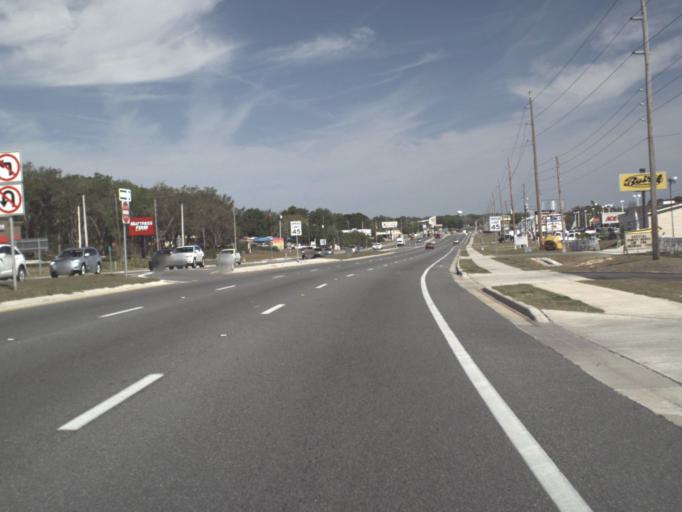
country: US
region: Florida
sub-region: Lake County
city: Fruitland Park
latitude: 28.8441
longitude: -81.8974
